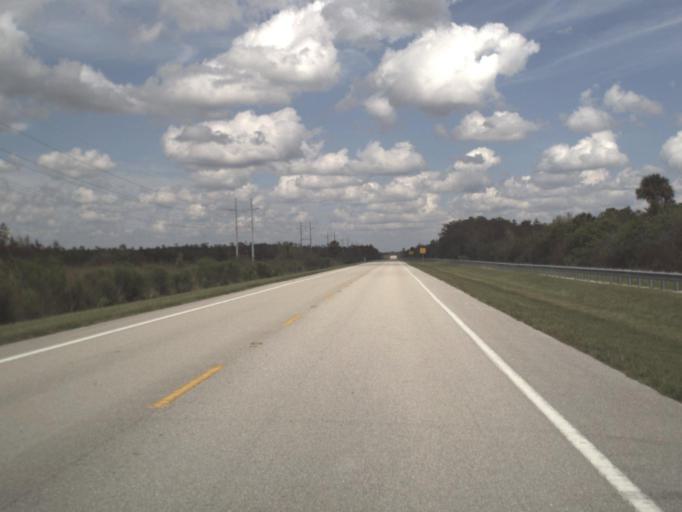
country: US
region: Florida
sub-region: Collier County
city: Lely Resort
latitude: 25.9661
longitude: -81.3532
